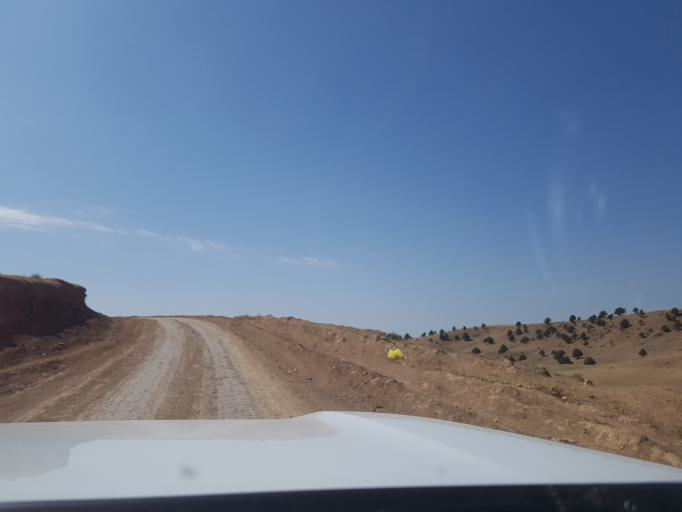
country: TM
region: Ahal
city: Baharly
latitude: 38.3237
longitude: 56.9538
